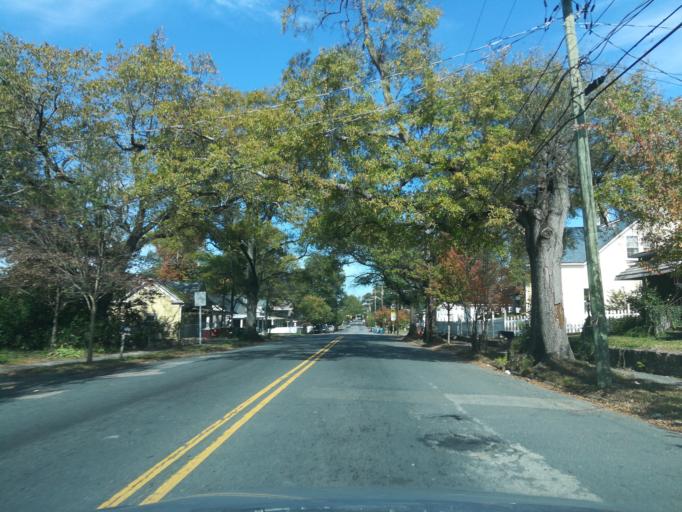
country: US
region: North Carolina
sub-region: Durham County
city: Durham
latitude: 35.9837
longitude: -78.8777
